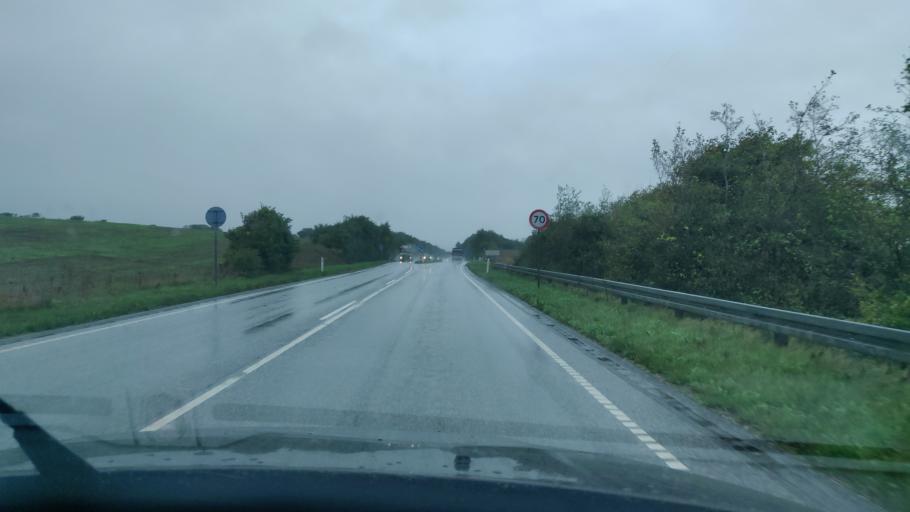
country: DK
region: North Denmark
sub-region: Thisted Kommune
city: Thisted
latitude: 56.9599
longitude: 8.6471
